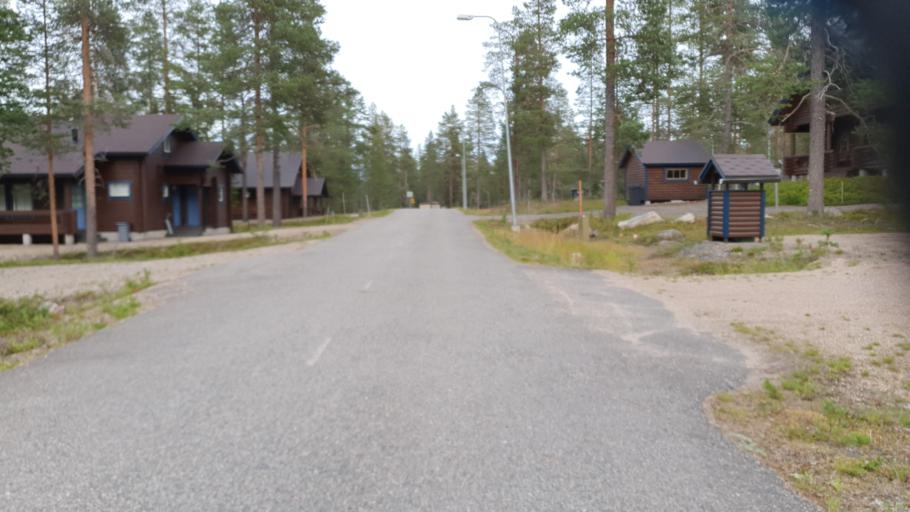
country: FI
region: Lapland
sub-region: Tunturi-Lappi
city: Kolari
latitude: 67.5926
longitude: 24.1536
